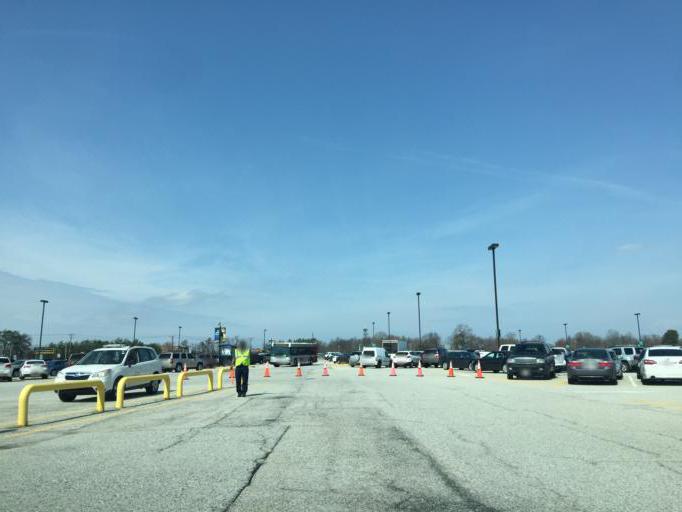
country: US
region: Maryland
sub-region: Anne Arundel County
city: Linthicum
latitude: 39.1909
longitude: -76.6596
